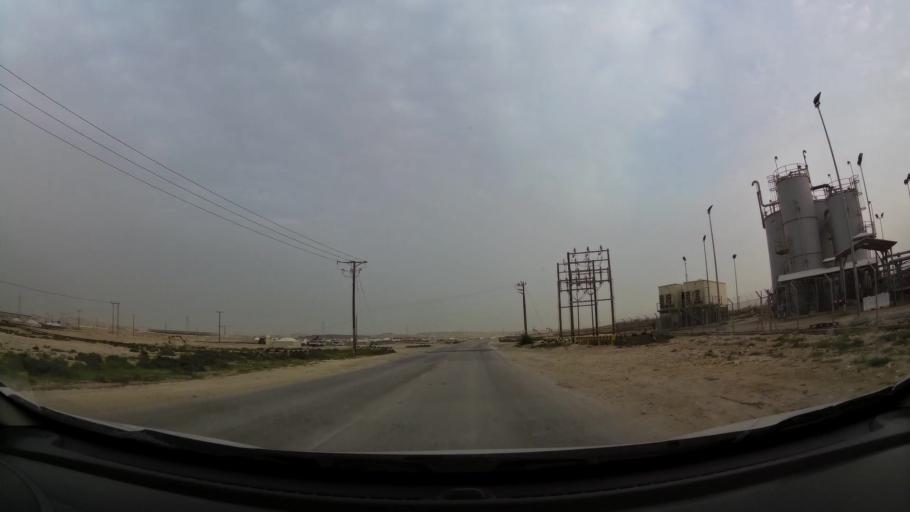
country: BH
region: Central Governorate
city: Dar Kulayb
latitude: 26.0171
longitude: 50.5752
